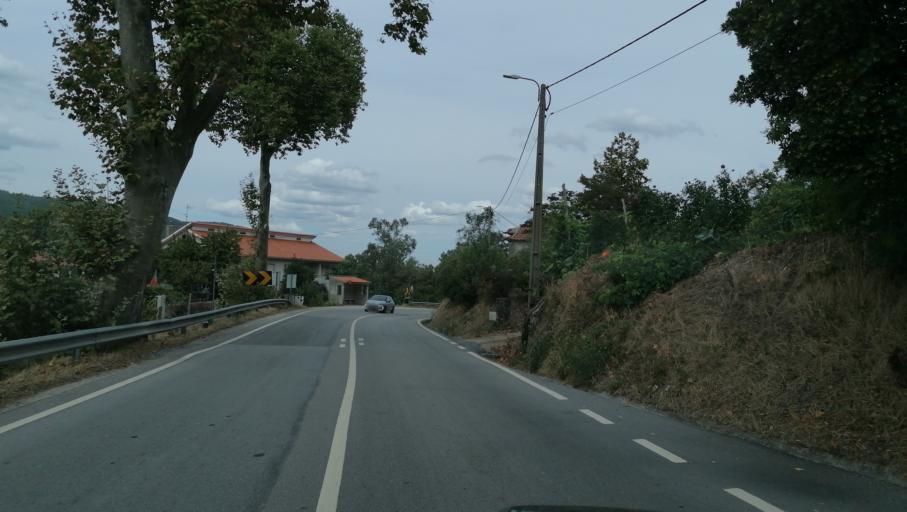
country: PT
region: Vila Real
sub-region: Vila Pouca de Aguiar
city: Vila Pouca de Aguiar
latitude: 41.5131
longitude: -7.6248
